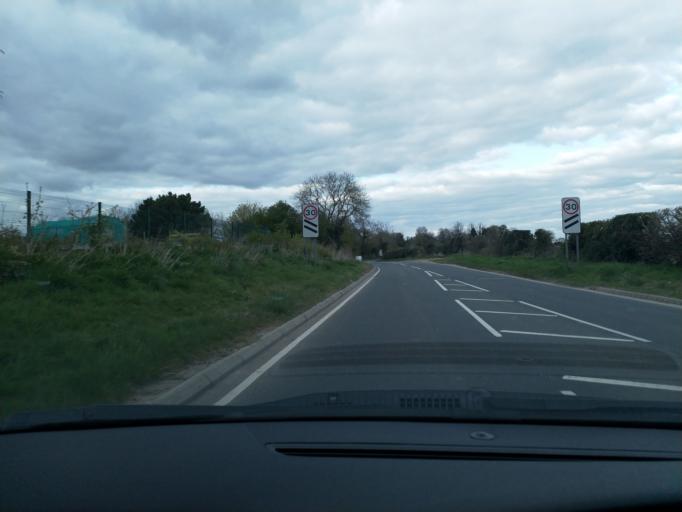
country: GB
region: England
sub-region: Warwickshire
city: Warwick
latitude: 52.2446
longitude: -1.5442
